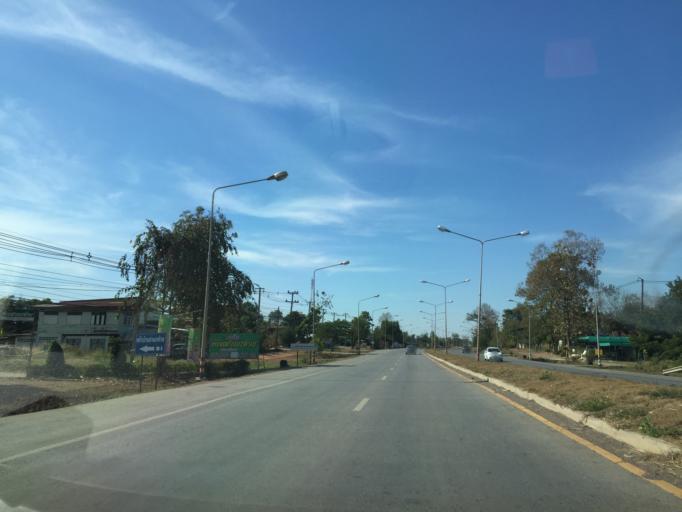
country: TH
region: Changwat Nong Bua Lamphu
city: Na Klang
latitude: 17.3042
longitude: 102.1942
